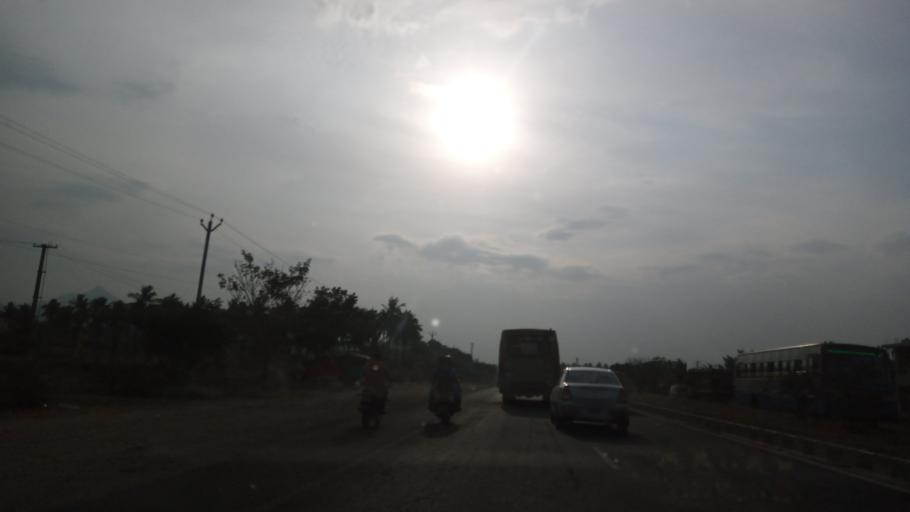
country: IN
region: Tamil Nadu
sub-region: Salem
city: Belur
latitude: 11.6649
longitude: 78.2966
